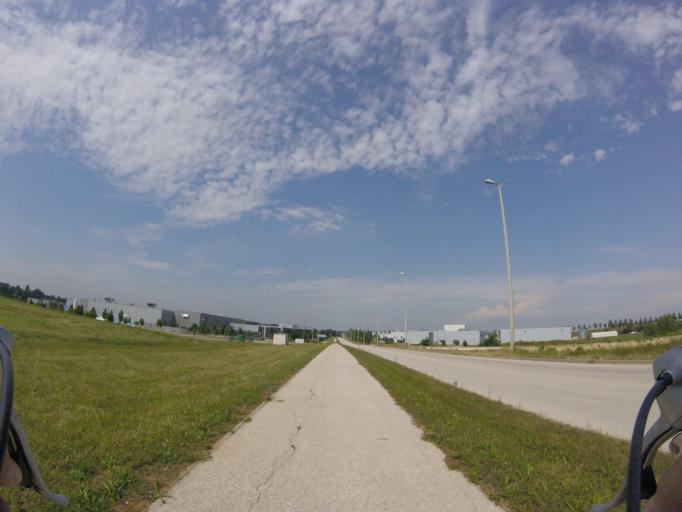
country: HU
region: Komarom-Esztergom
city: Kornye
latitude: 47.5844
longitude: 18.3387
